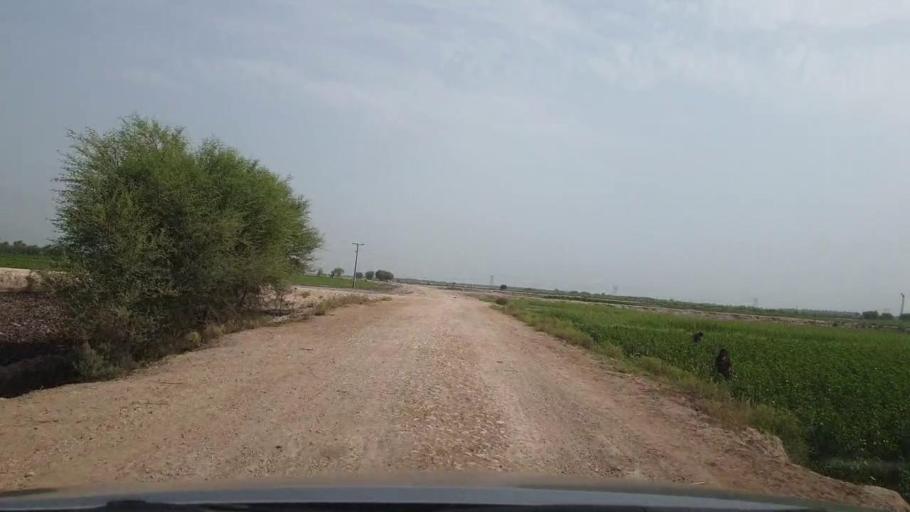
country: PK
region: Sindh
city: Rohri
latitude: 27.6607
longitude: 69.0255
